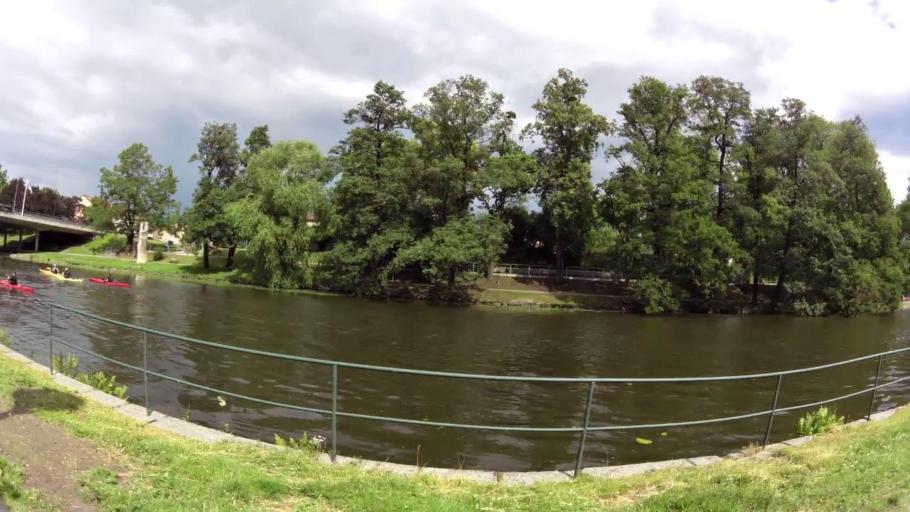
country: SE
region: OEstergoetland
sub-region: Linkopings Kommun
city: Linkoping
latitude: 58.4090
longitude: 15.6339
